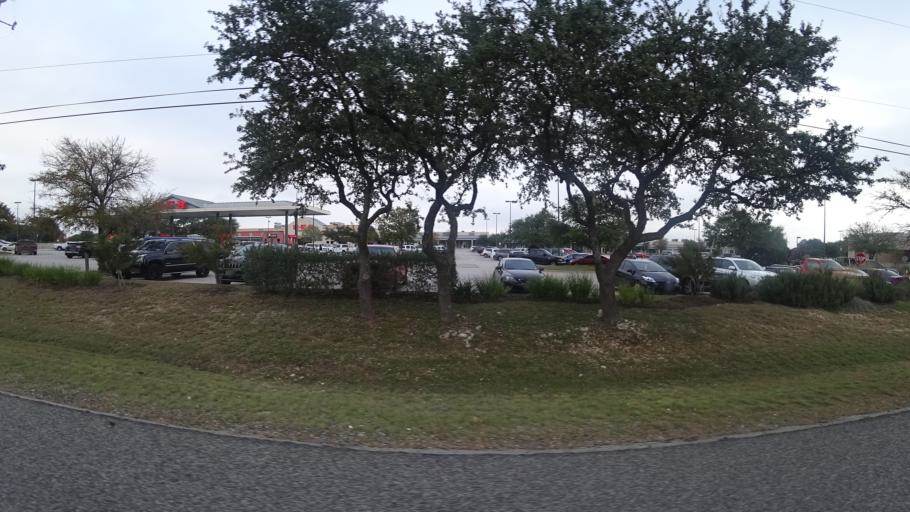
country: US
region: Texas
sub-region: Travis County
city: Bee Cave
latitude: 30.3031
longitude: -97.9326
